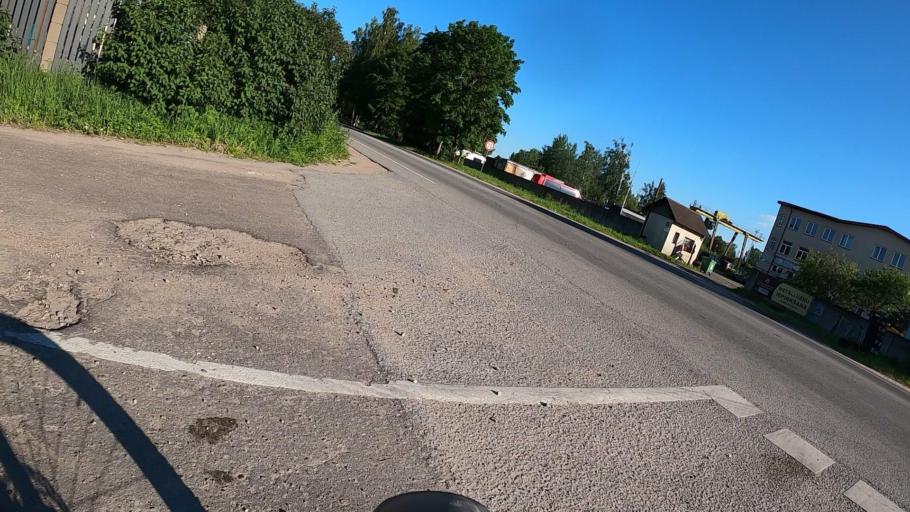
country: LV
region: Kekava
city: Kekava
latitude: 56.9007
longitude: 24.2263
